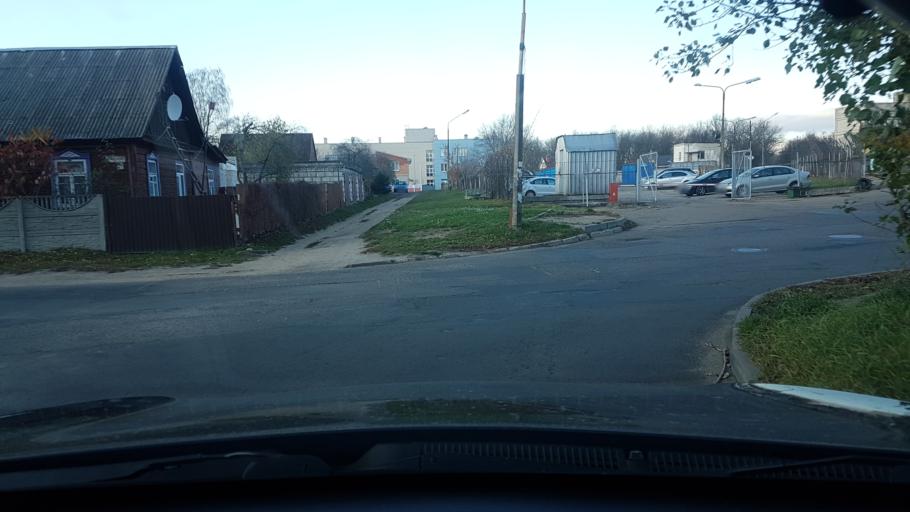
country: BY
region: Minsk
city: Minsk
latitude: 53.9360
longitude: 27.5413
